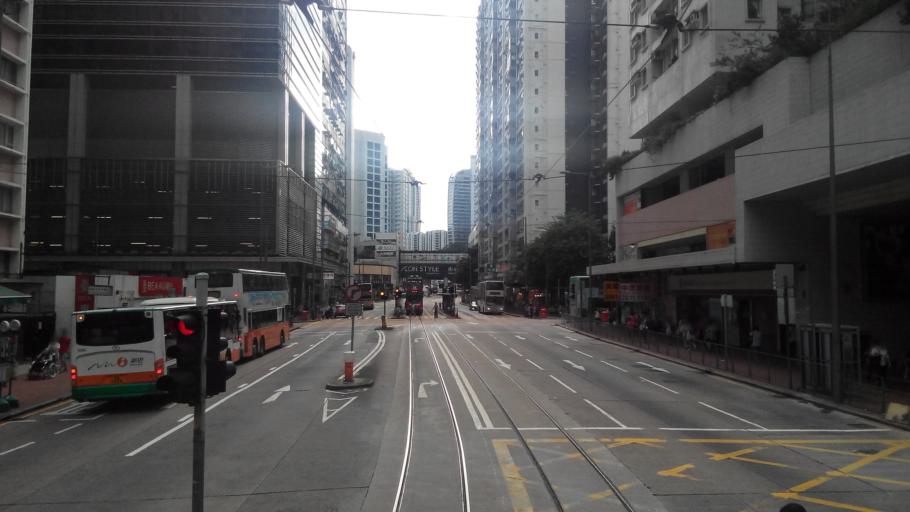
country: HK
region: Wanchai
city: Wan Chai
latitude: 22.2846
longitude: 114.2130
